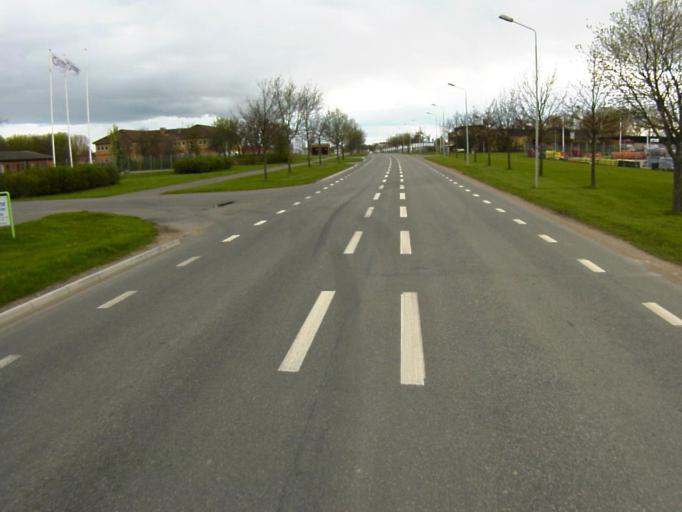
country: SE
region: Skane
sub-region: Kristianstads Kommun
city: Kristianstad
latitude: 56.0540
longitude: 14.1660
